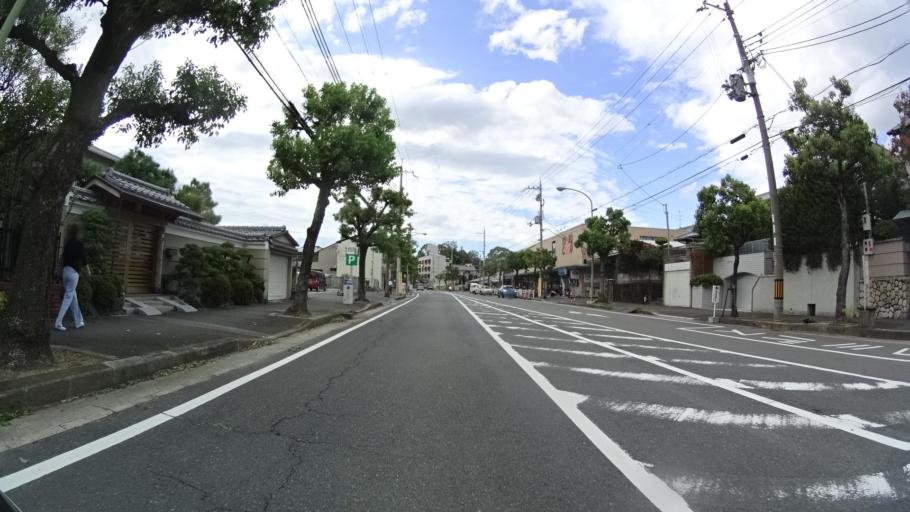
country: JP
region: Kyoto
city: Yawata
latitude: 34.8681
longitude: 135.6920
